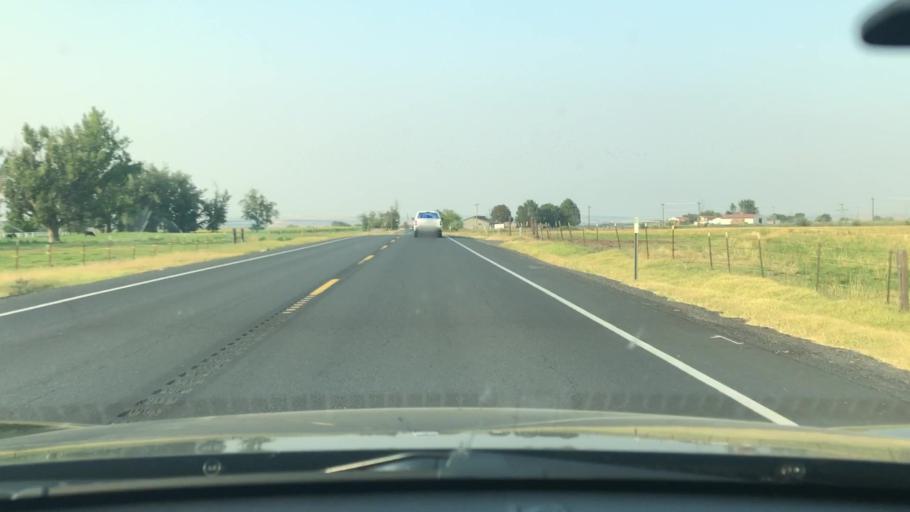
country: US
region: Oregon
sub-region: Umatilla County
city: Hermiston
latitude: 45.8911
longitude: -119.1864
